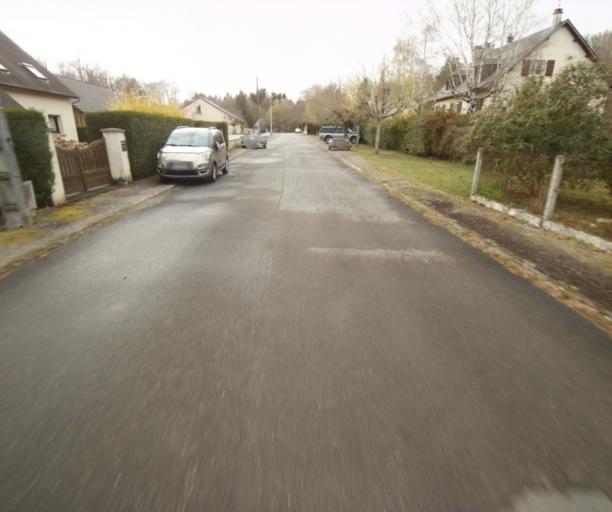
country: FR
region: Limousin
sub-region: Departement de la Correze
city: Saint-Privat
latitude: 45.2159
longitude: 2.0058
